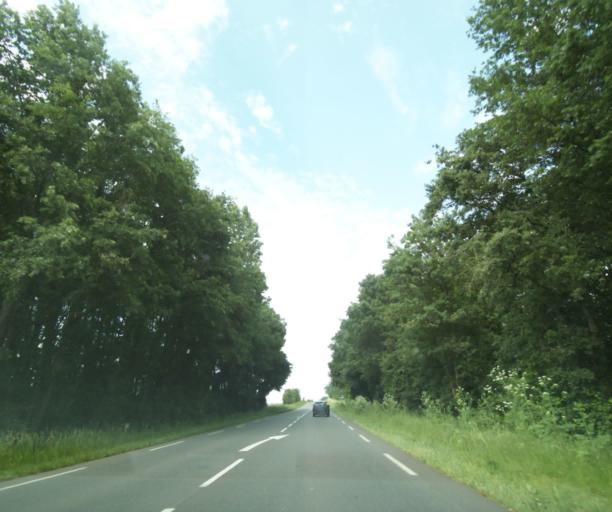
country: FR
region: Pays de la Loire
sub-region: Departement de Maine-et-Loire
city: Montreuil-Bellay
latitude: 47.1709
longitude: -0.1384
